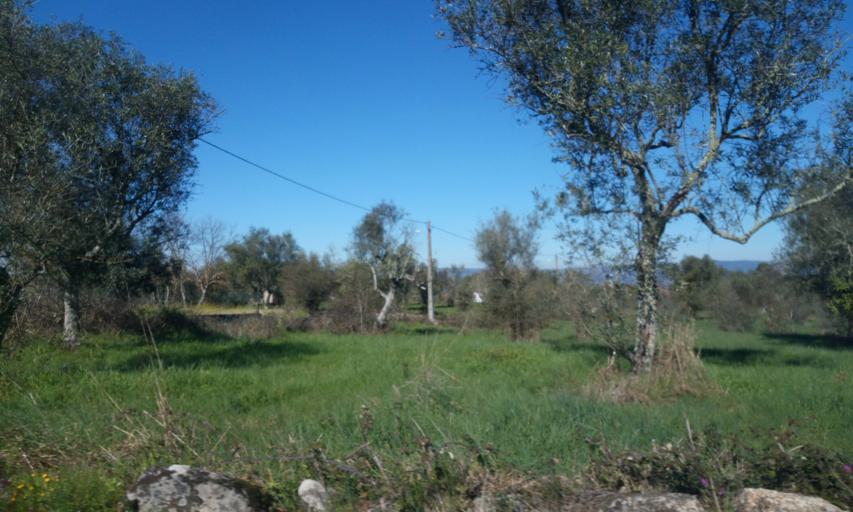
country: PT
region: Guarda
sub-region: Fornos de Algodres
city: Fornos de Algodres
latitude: 40.5261
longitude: -7.5575
